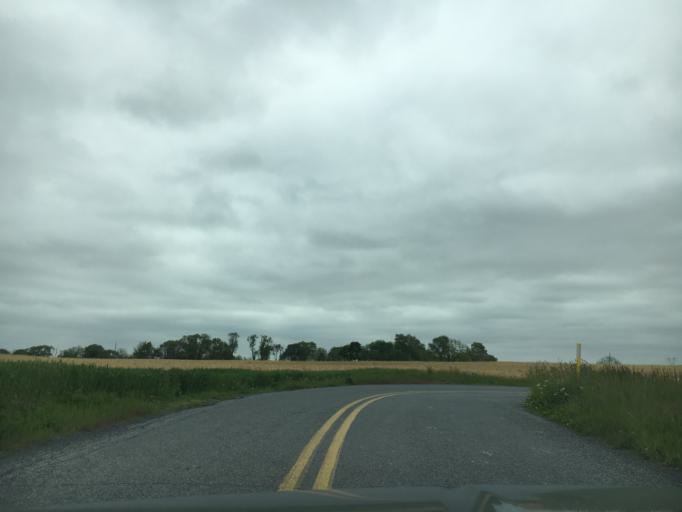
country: US
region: Pennsylvania
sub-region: Berks County
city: Fleetwood
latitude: 40.4838
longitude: -75.8289
